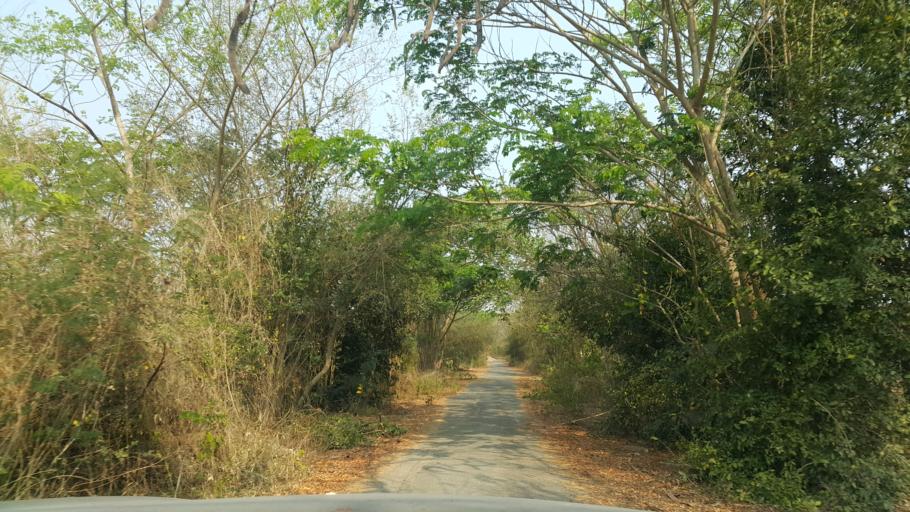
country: TH
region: Chiang Mai
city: San Kamphaeng
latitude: 18.7620
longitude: 99.1118
